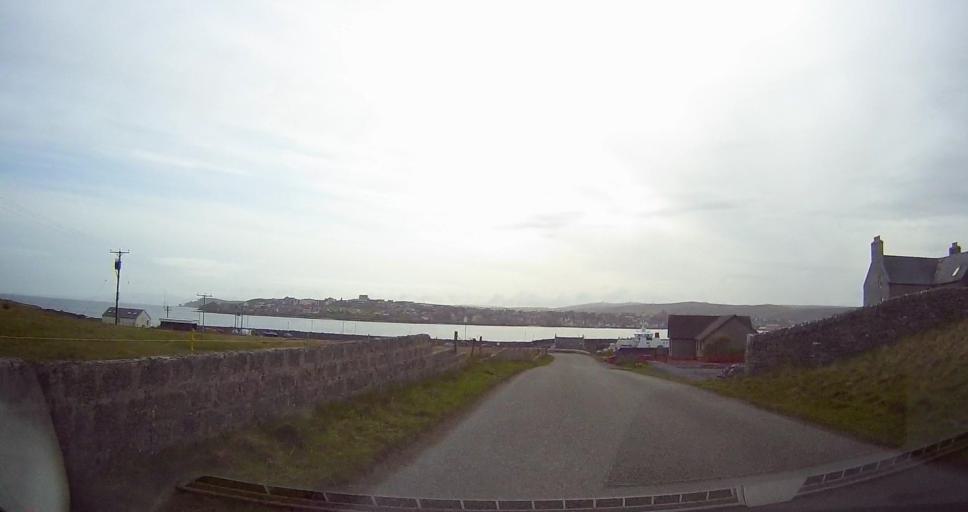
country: GB
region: Scotland
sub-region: Shetland Islands
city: Shetland
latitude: 60.1578
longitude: -1.1198
